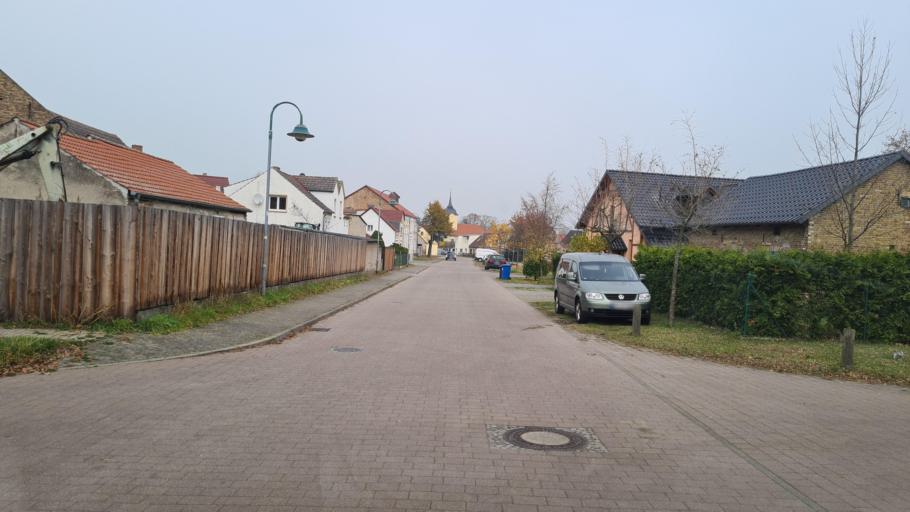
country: DE
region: Brandenburg
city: Golzow
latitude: 52.3491
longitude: 12.6274
